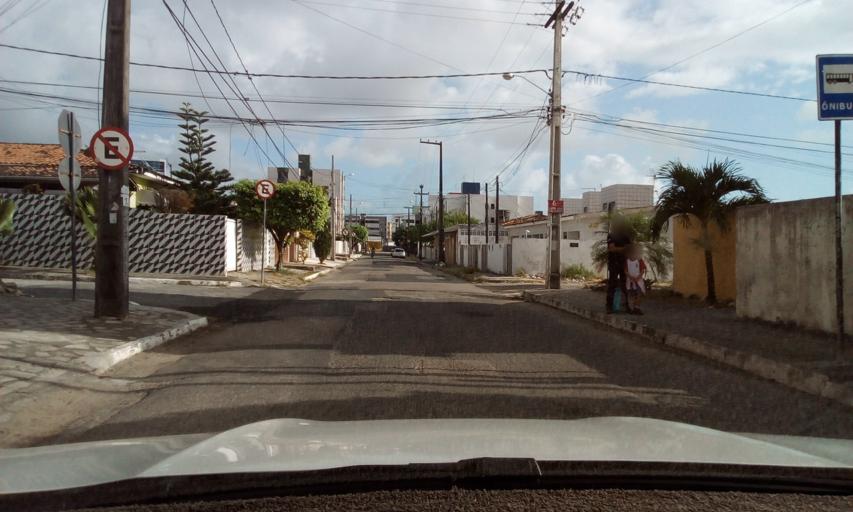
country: BR
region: Paraiba
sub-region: Joao Pessoa
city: Joao Pessoa
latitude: -7.1513
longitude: -34.8490
